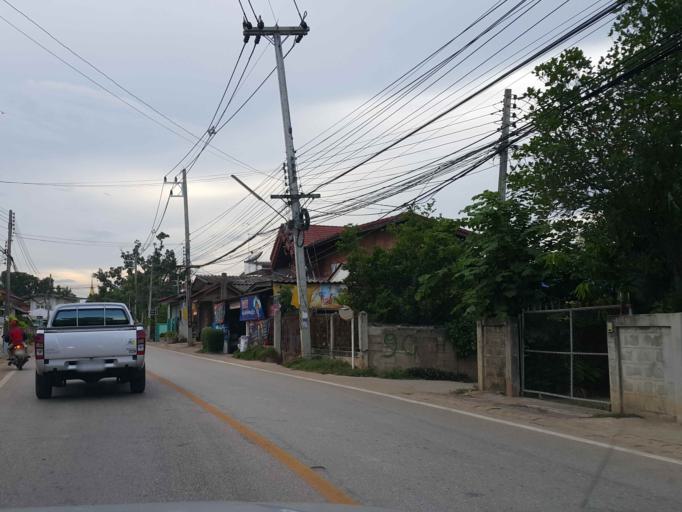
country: TH
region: Lampang
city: Hang Chat
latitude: 18.3090
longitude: 99.3645
